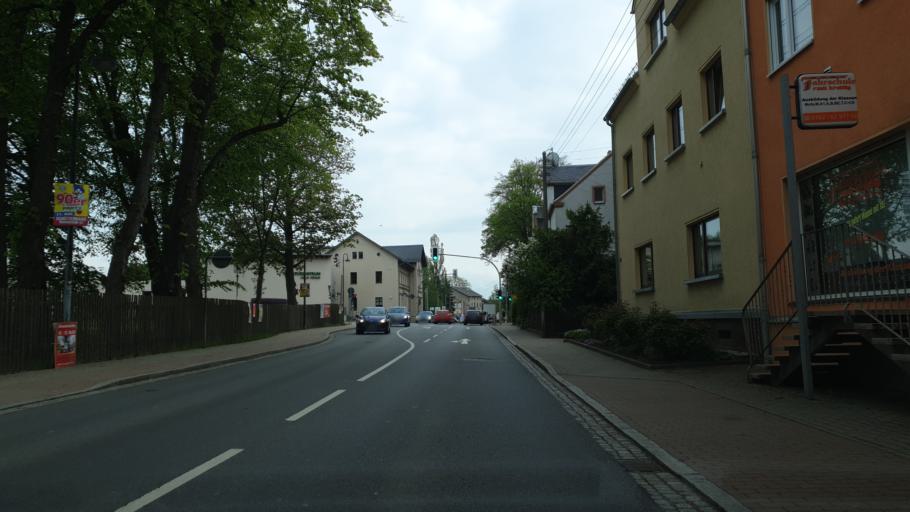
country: DE
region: Saxony
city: Lugau
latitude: 50.7427
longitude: 12.7467
